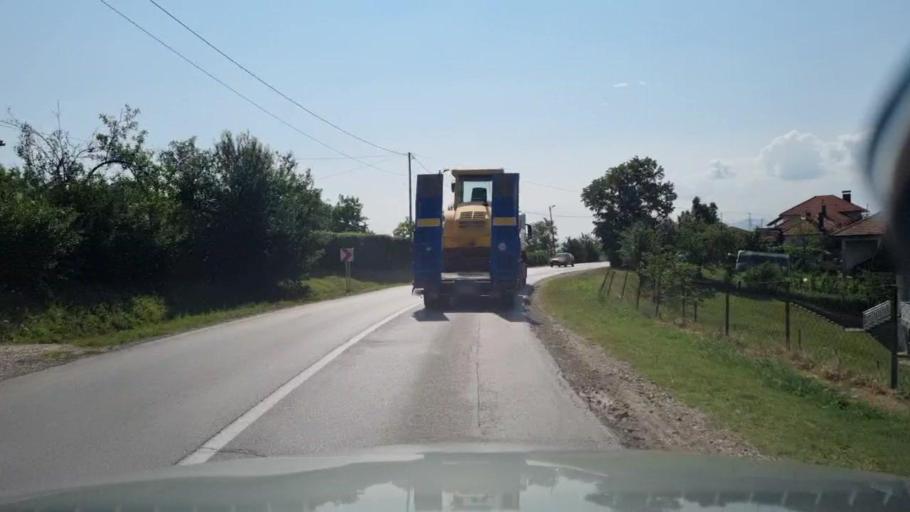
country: BA
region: Federation of Bosnia and Herzegovina
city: Mionica
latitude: 44.8458
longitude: 18.4417
